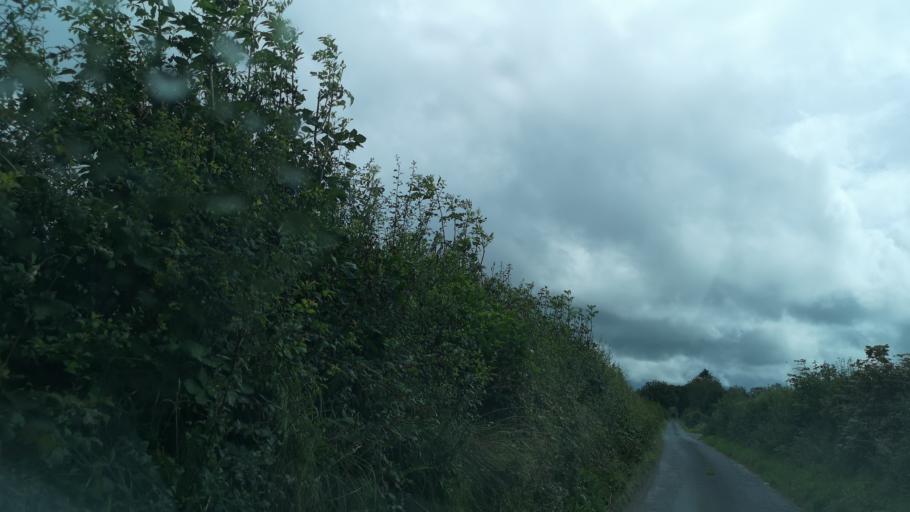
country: IE
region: Connaught
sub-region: County Galway
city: Loughrea
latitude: 53.3030
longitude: -8.5935
